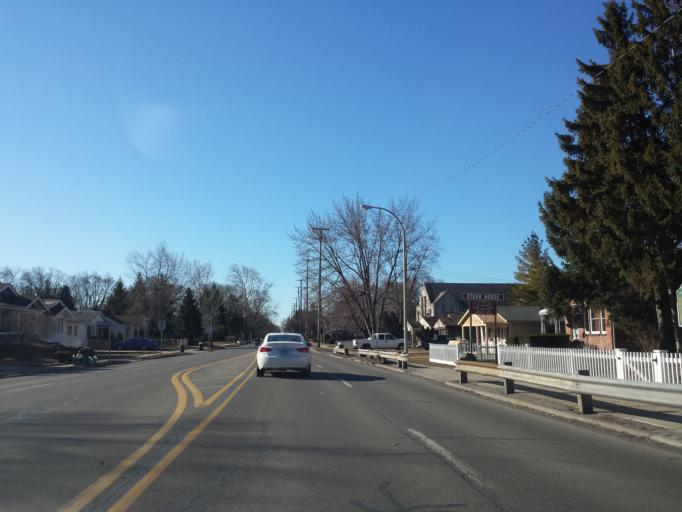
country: US
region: Michigan
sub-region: Oakland County
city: Clawson
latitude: 42.5183
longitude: -83.1456
